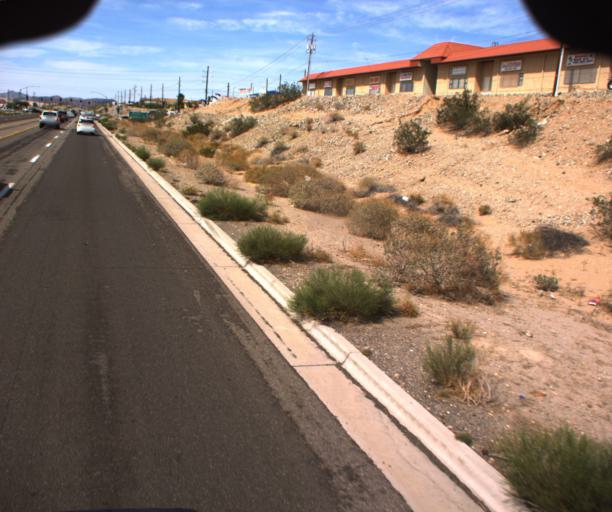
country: US
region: Arizona
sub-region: Mohave County
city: Lake Havasu City
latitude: 34.5005
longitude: -114.3493
